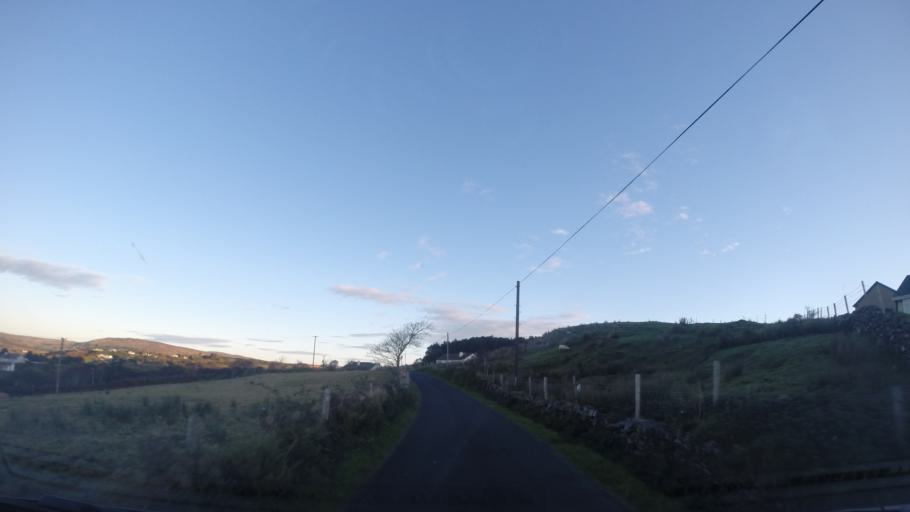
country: IE
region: Ulster
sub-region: County Donegal
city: Killybegs
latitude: 54.6358
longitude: -8.6252
